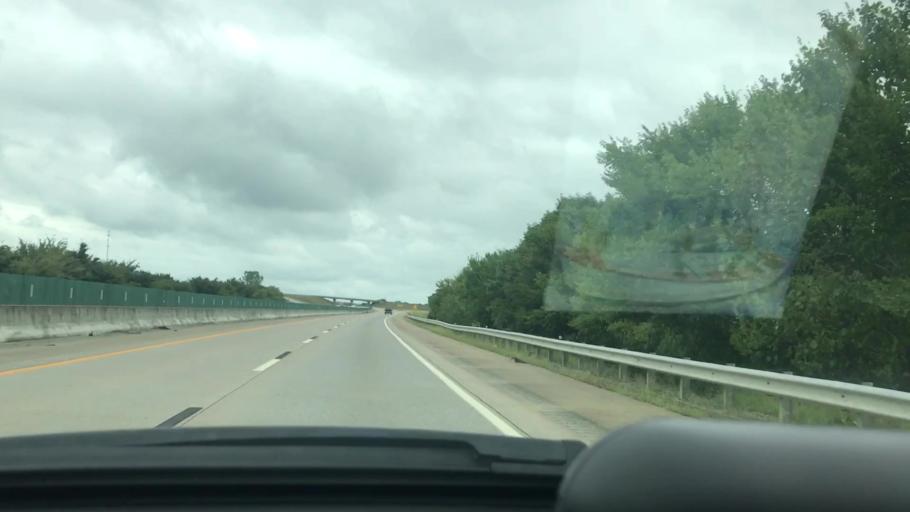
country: US
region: Oklahoma
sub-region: Pittsburg County
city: Krebs
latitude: 35.0514
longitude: -95.7089
